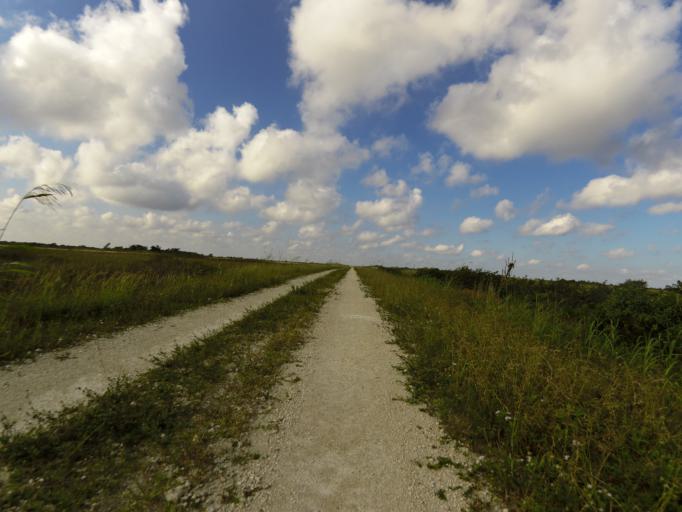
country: US
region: Florida
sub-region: Broward County
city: Weston
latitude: 26.0564
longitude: -80.4566
